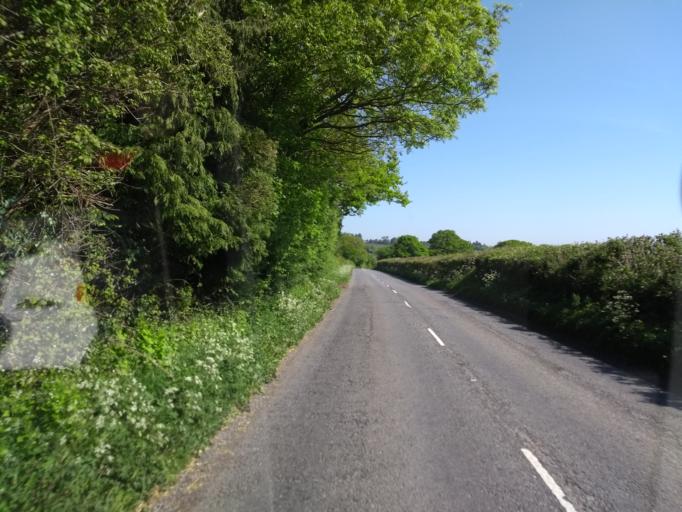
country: GB
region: England
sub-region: Devon
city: Axminster
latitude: 50.8116
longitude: -2.9759
